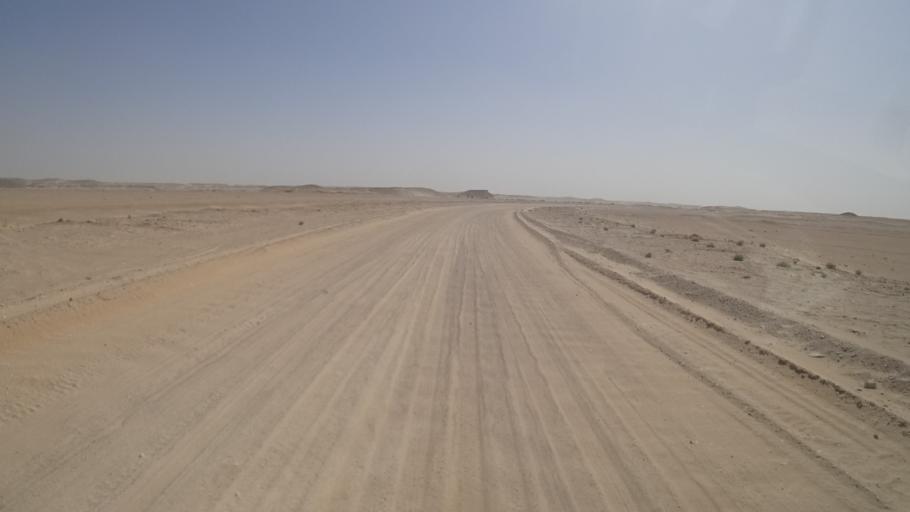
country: YE
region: Al Mahrah
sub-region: Shahan
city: Shihan as Sufla
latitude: 17.8853
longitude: 52.6055
